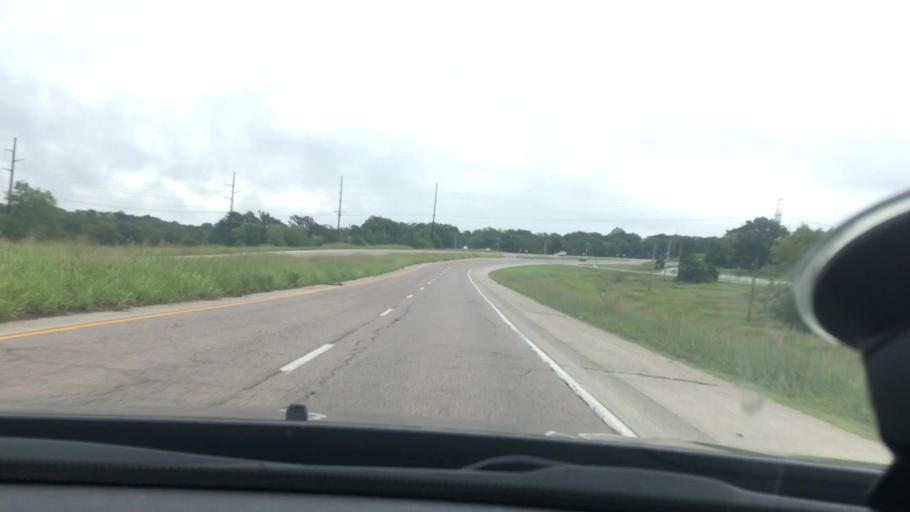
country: US
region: Oklahoma
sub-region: Pontotoc County
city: Ada
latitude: 34.7814
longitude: -96.6041
